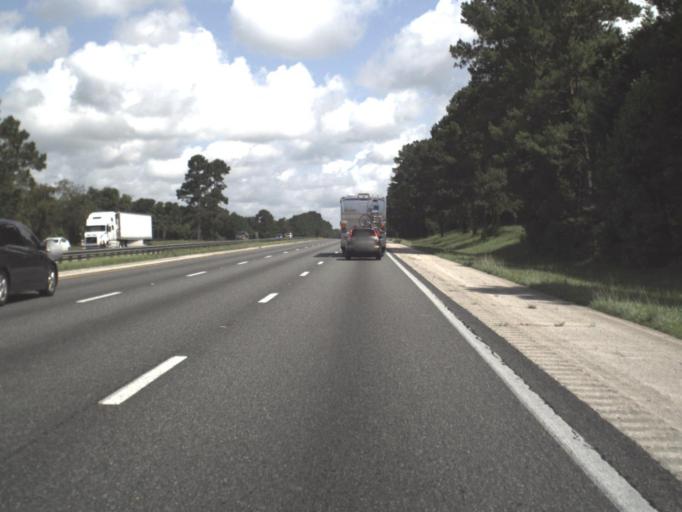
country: US
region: Florida
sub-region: Alachua County
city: High Springs
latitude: 29.8259
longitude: -82.5206
